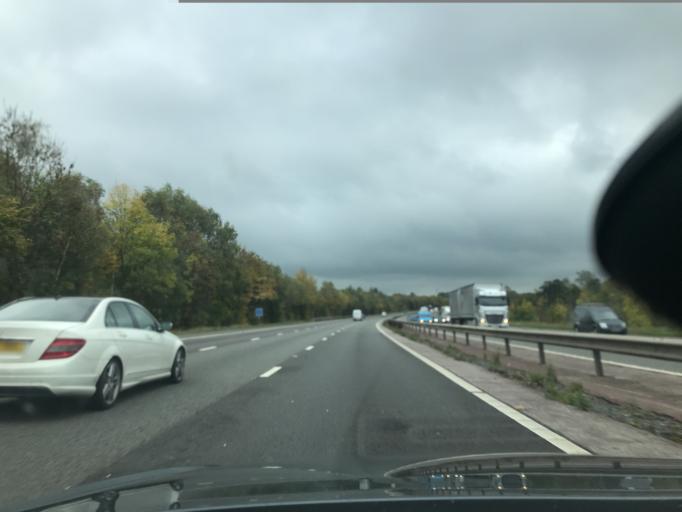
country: GB
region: England
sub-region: Warwickshire
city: Wroxall
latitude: 52.3239
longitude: -1.7261
